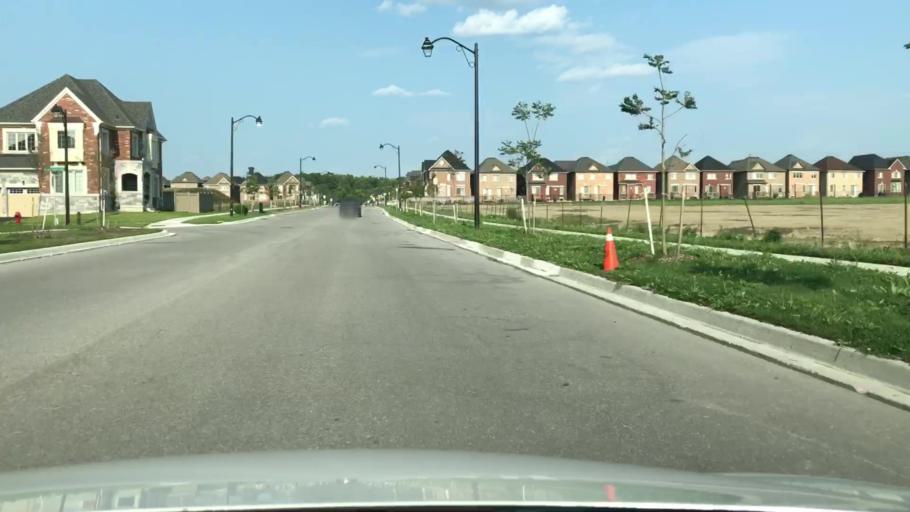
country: CA
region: Ontario
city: Newmarket
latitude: 44.0215
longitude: -79.4355
